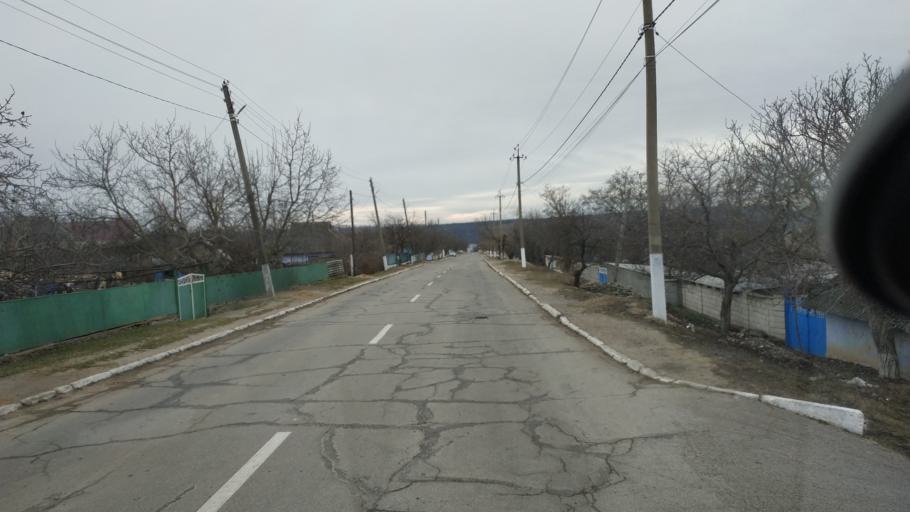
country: MD
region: Telenesti
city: Cocieri
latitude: 47.3514
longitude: 29.1170
